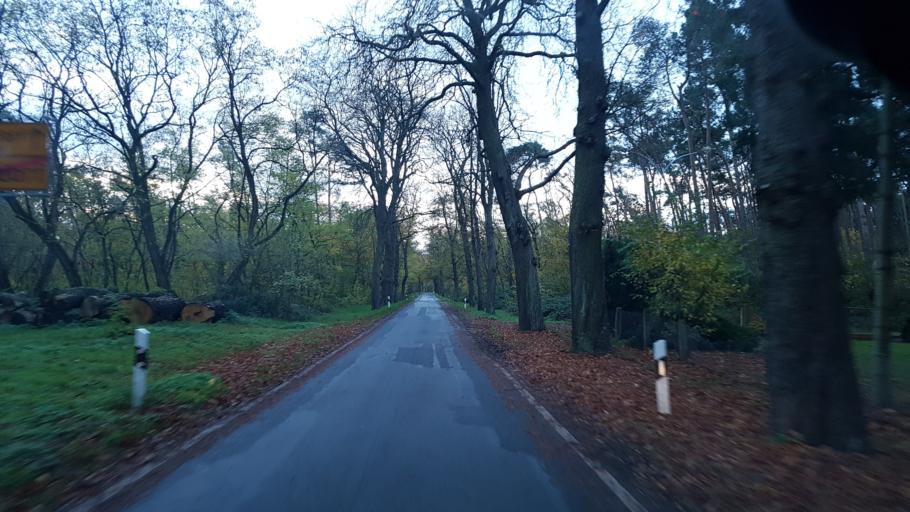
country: DE
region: Brandenburg
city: Muhlberg
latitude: 51.4859
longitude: 13.2291
